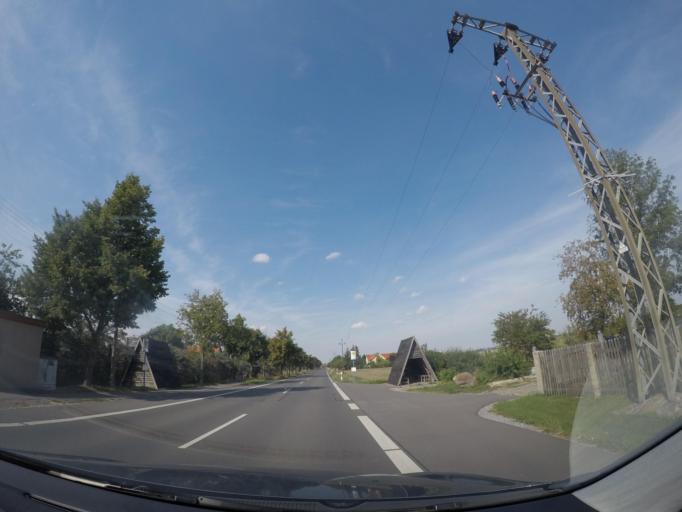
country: DE
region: Saxony-Anhalt
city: Langeln
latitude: 51.8814
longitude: 10.7703
